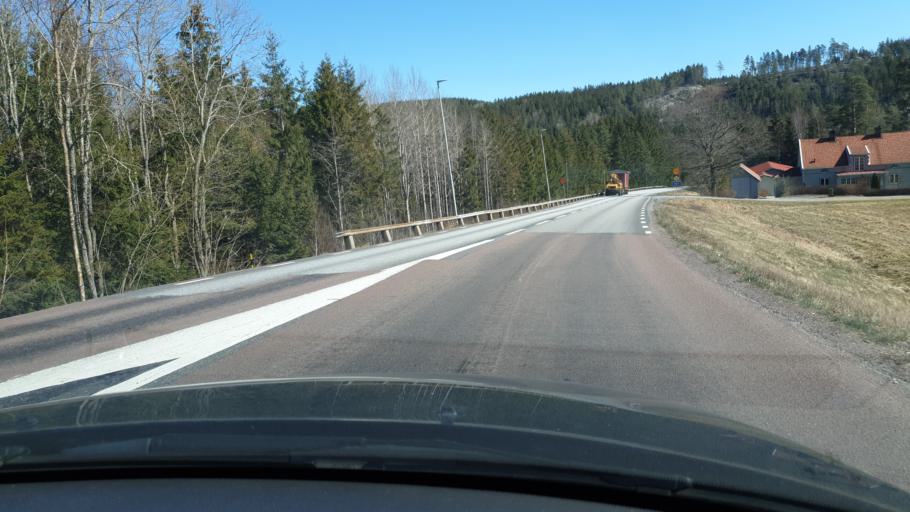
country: SE
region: Vaestra Goetaland
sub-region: Tanums Kommun
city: Tanumshede
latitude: 58.7968
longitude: 11.5620
